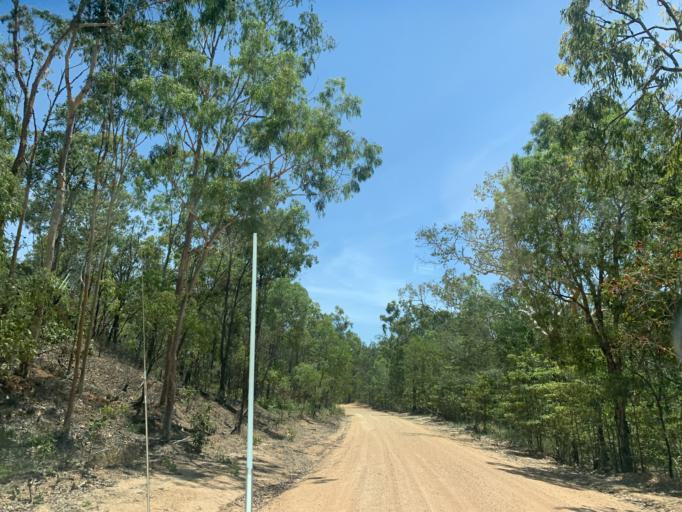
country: AU
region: Queensland
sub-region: Tablelands
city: Kuranda
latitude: -16.9183
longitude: 145.5942
